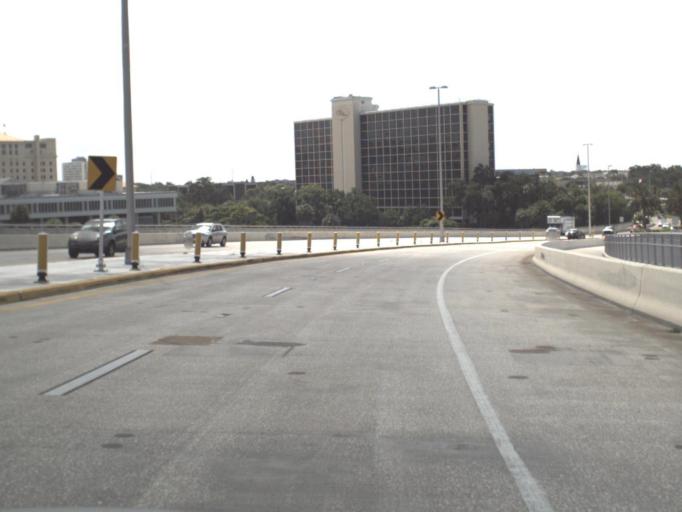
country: US
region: Florida
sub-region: Pinellas County
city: Clearwater
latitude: 27.9654
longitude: -82.8044
